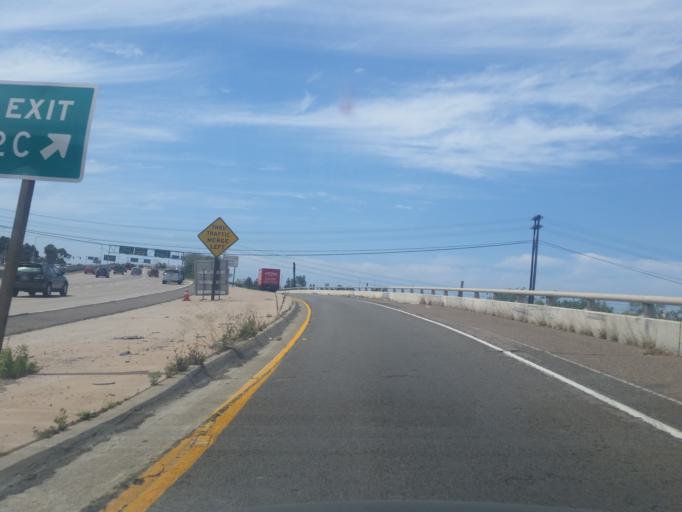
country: US
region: California
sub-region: San Diego County
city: San Diego
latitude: 32.7609
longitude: -117.1945
